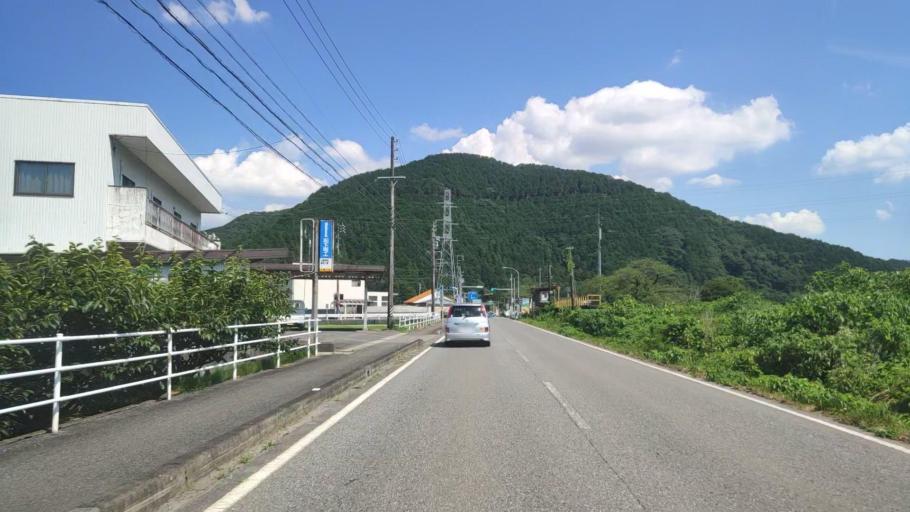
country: JP
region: Gifu
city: Godo
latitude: 35.5182
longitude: 136.6496
